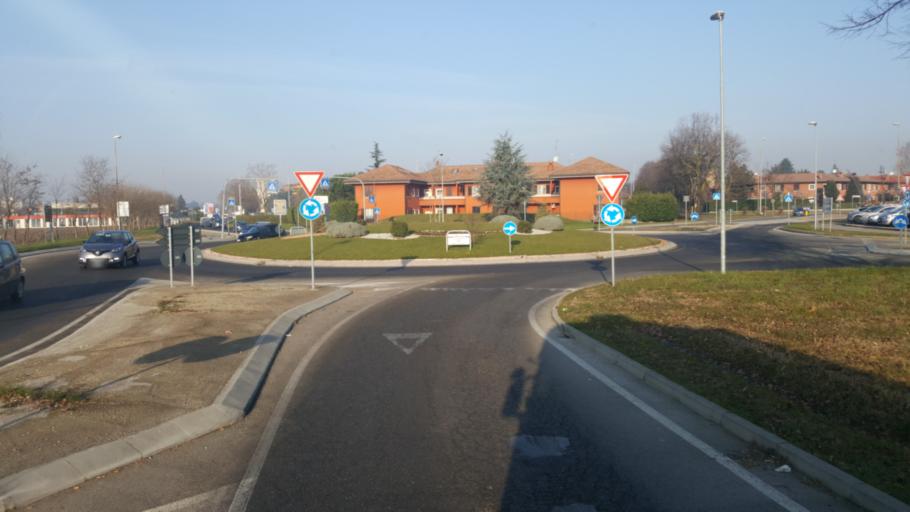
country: IT
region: Lombardy
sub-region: Citta metropolitana di Milano
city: Inzago
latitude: 45.5345
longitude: 9.4905
